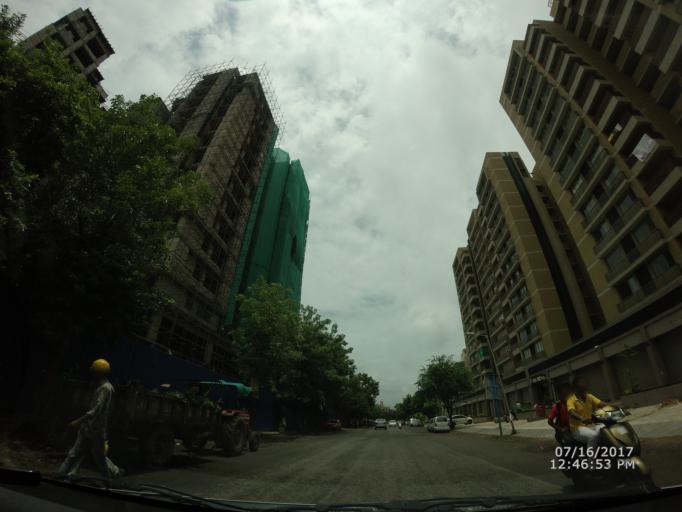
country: IN
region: Gujarat
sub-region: Ahmadabad
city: Sarkhej
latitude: 23.0189
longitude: 72.5161
